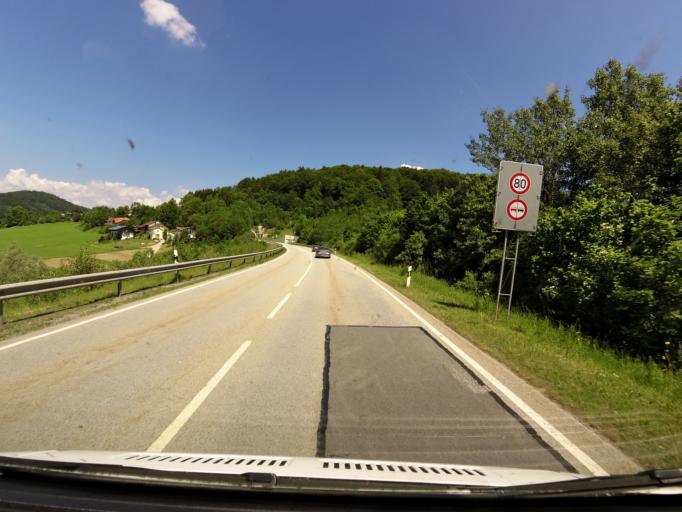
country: DE
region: Bavaria
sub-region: Lower Bavaria
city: Ringelai
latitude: 48.7831
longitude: 13.5068
